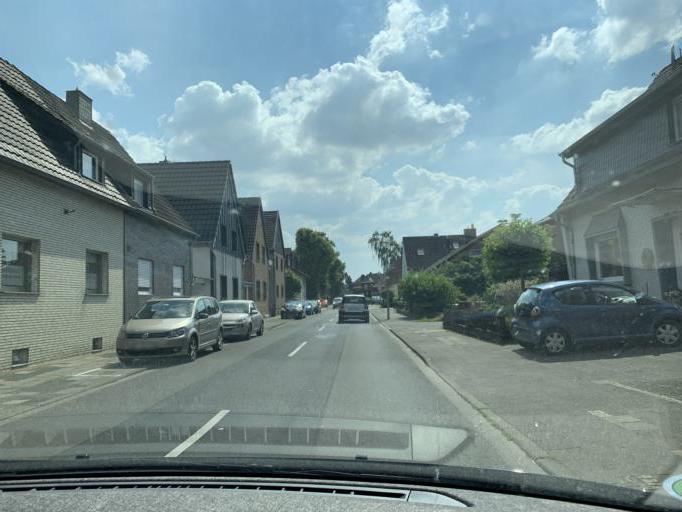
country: DE
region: North Rhine-Westphalia
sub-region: Regierungsbezirk Koln
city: Elsdorf
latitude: 50.9271
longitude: 6.5922
